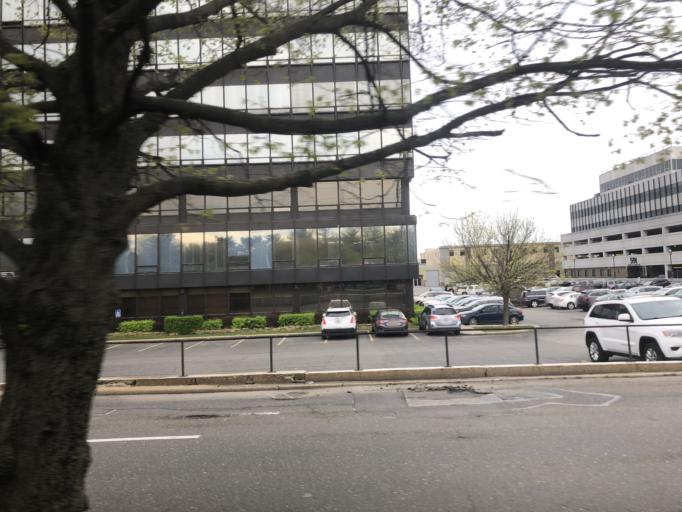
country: US
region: New York
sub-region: Nassau County
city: East Garden City
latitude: 40.7325
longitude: -73.6131
